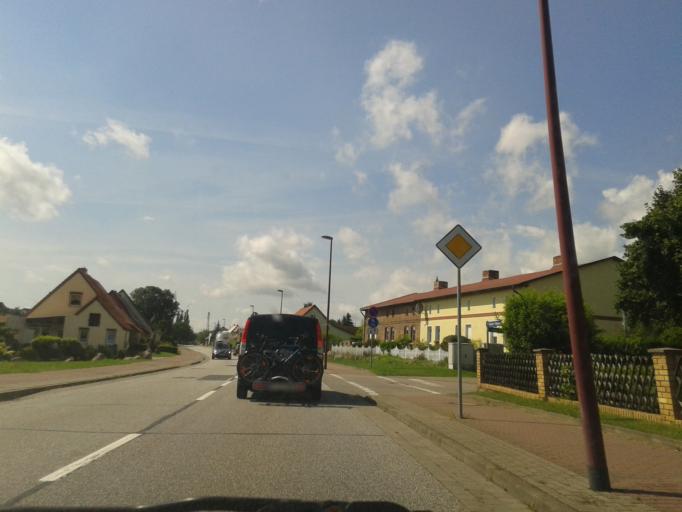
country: DE
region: Mecklenburg-Vorpommern
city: Pasewalk
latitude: 53.4725
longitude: 13.9777
